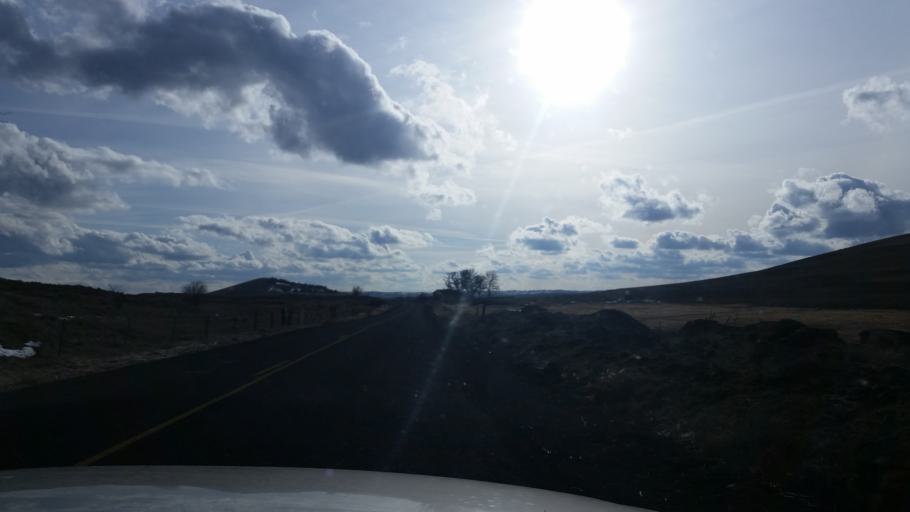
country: US
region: Washington
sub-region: Spokane County
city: Cheney
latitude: 47.3019
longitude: -117.6269
